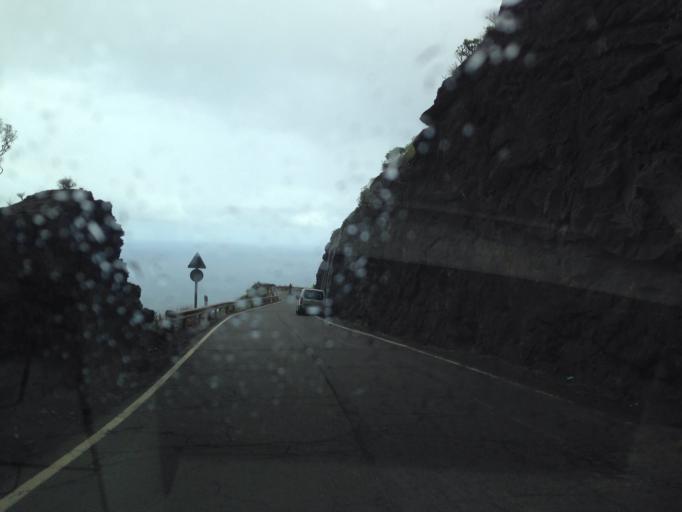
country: ES
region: Canary Islands
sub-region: Provincia de Las Palmas
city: San Nicolas
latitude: 28.0372
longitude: -15.7492
